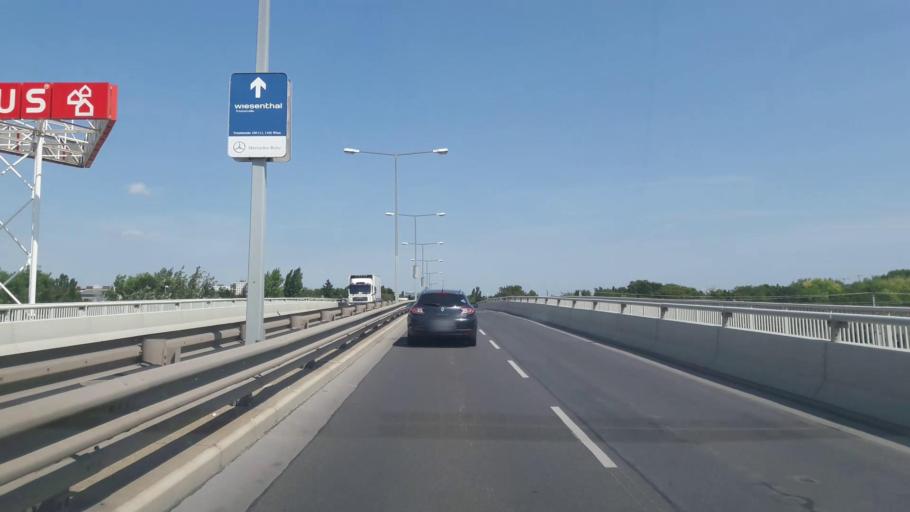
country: AT
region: Lower Austria
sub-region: Politischer Bezirk Modling
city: Vosendorf
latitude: 48.1501
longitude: 16.3623
